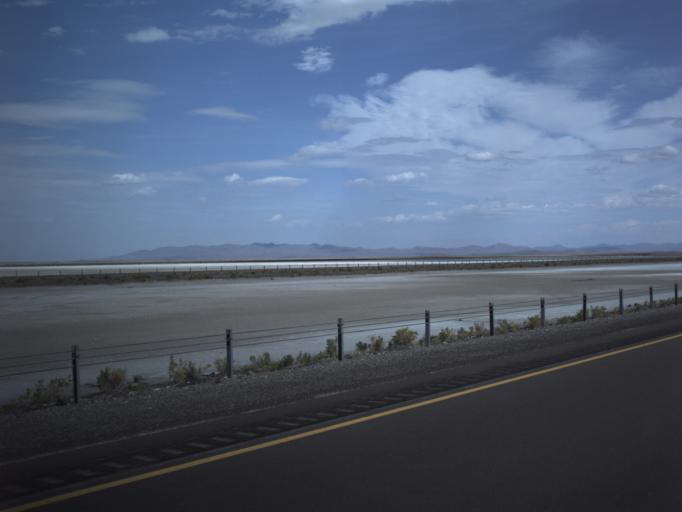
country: US
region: Utah
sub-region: Tooele County
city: Wendover
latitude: 40.7280
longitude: -113.3764
